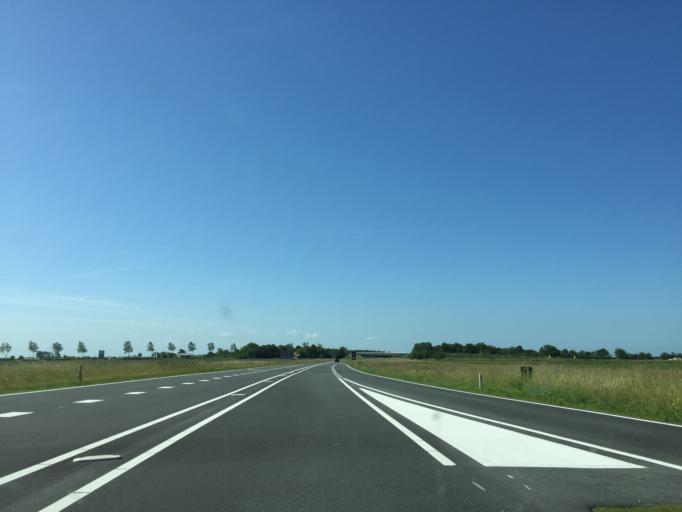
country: NL
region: Zeeland
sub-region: Schouwen-Duiveland
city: Scharendijke
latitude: 51.7294
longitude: 3.8236
